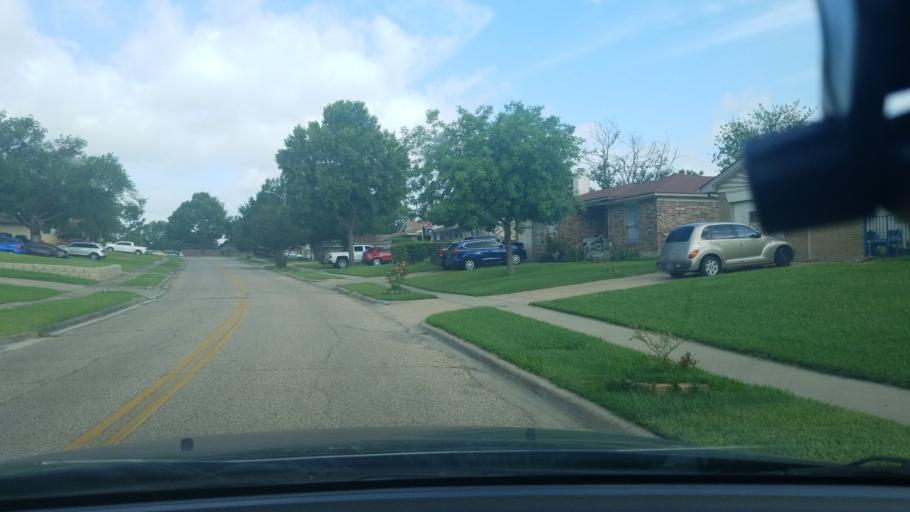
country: US
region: Texas
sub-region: Dallas County
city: Mesquite
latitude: 32.7735
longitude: -96.6332
